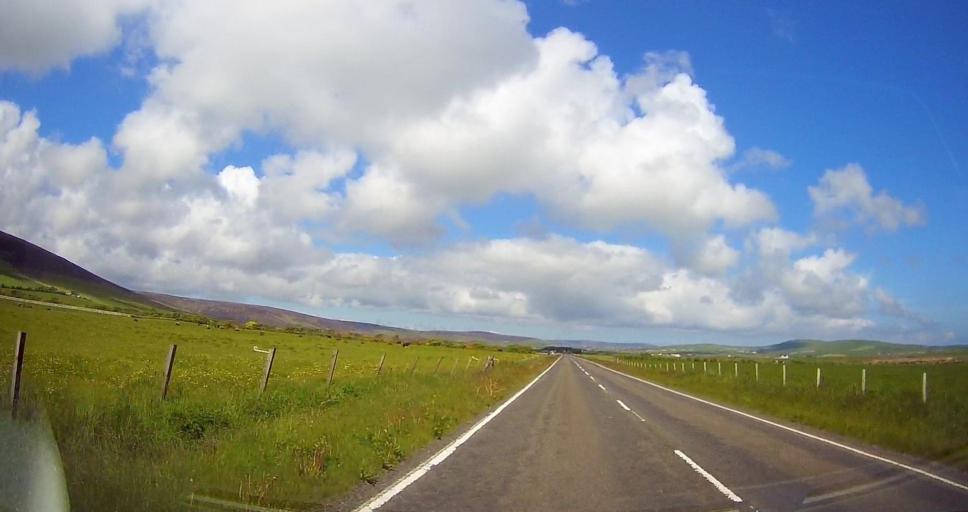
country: GB
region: Scotland
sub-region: Orkney Islands
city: Orkney
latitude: 59.0333
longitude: -3.0910
